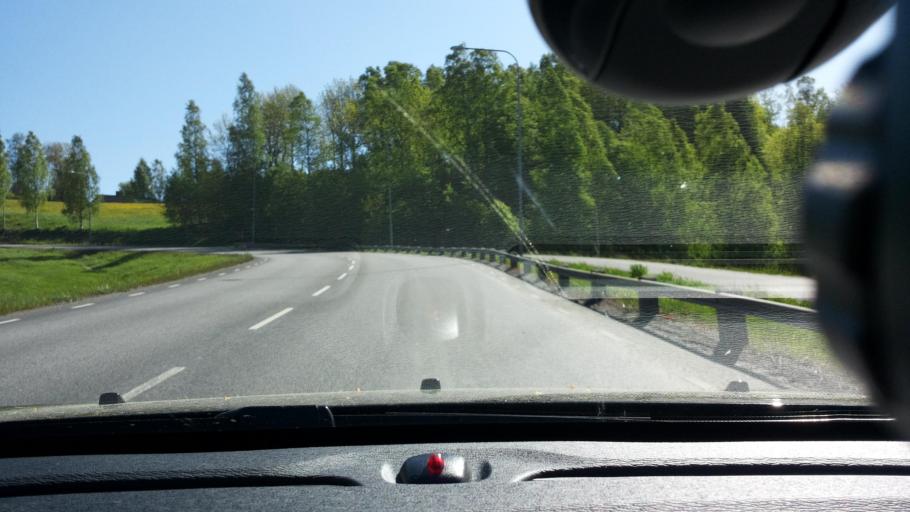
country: SE
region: Vaesternorrland
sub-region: Timra Kommun
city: Timra
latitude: 62.4777
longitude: 17.3150
